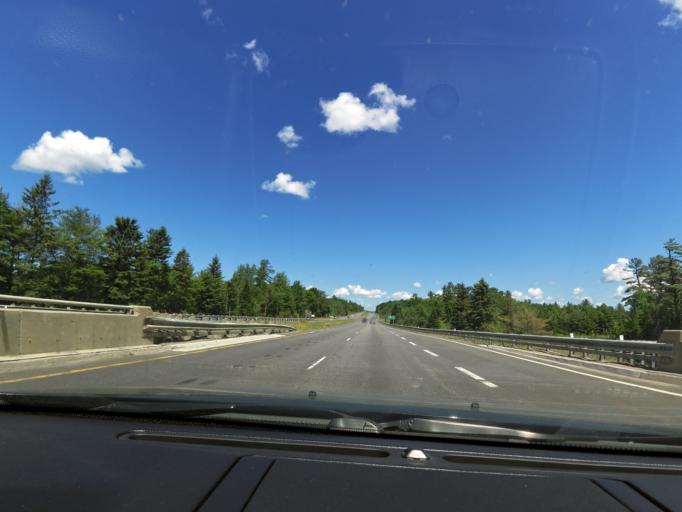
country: CA
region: Ontario
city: Bracebridge
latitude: 45.0884
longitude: -79.2997
